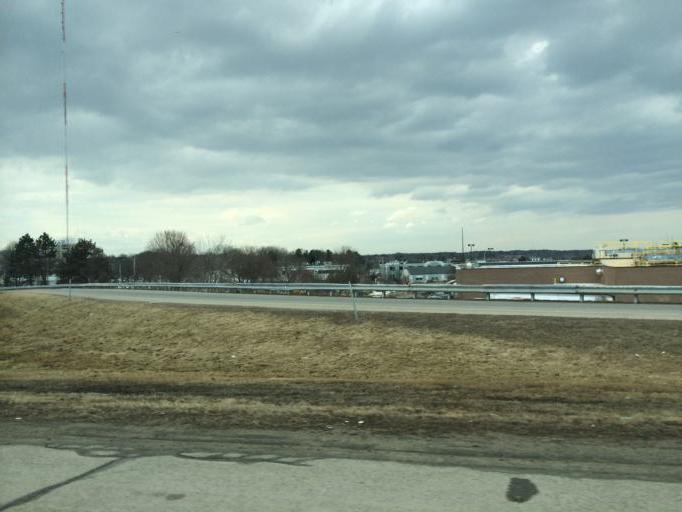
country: KZ
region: Zhambyl
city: Zhangatas
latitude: 43.6626
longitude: 70.2682
